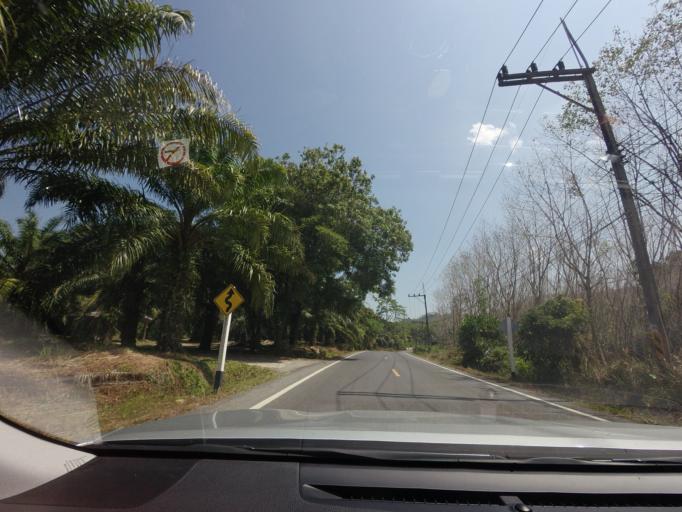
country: TH
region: Phangnga
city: Takua Thung
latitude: 8.2514
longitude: 98.3977
